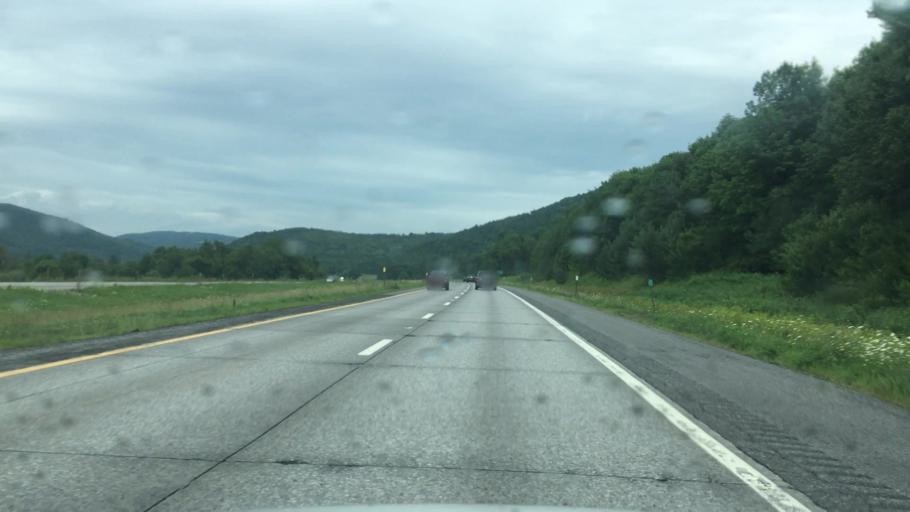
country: US
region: New York
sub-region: Otsego County
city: Worcester
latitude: 42.5608
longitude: -74.7781
